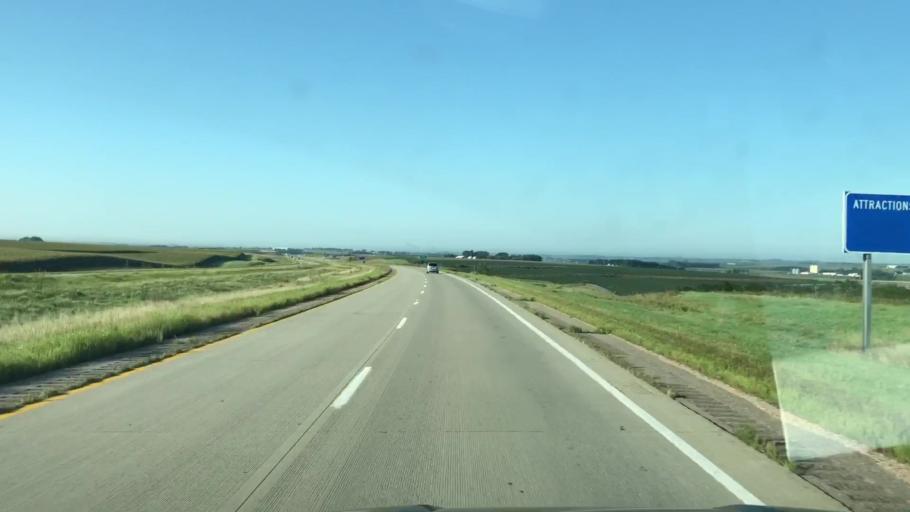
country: US
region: Iowa
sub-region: Plymouth County
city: Le Mars
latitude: 42.8084
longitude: -96.1978
